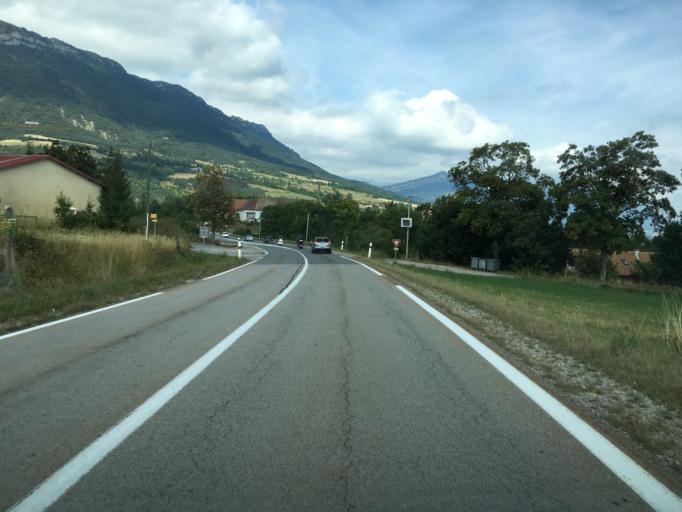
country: FR
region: Rhone-Alpes
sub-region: Departement de l'Isere
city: Mens
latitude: 44.7865
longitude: 5.6460
